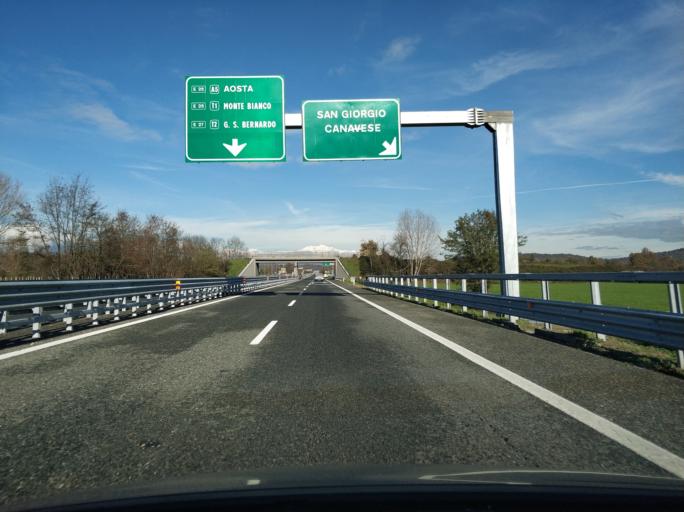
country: IT
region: Piedmont
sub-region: Provincia di Torino
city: San Giusto Canavese
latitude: 45.3124
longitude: 7.8197
